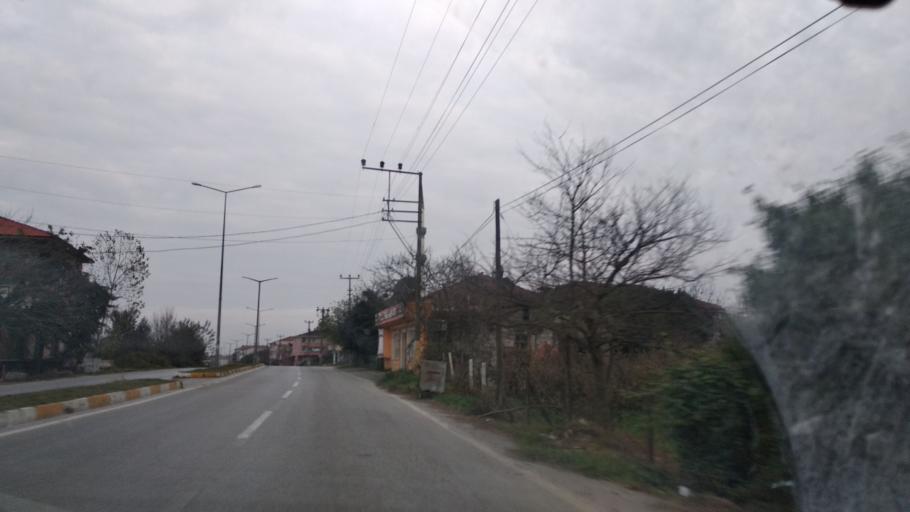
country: TR
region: Sakarya
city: Karasu
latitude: 41.0984
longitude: 30.6732
